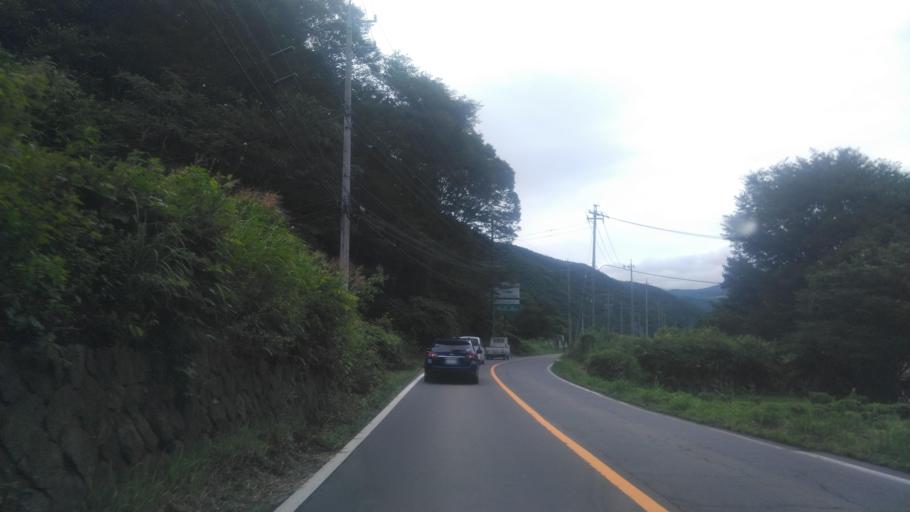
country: JP
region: Nagano
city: Ueda
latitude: 36.4699
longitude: 138.3429
